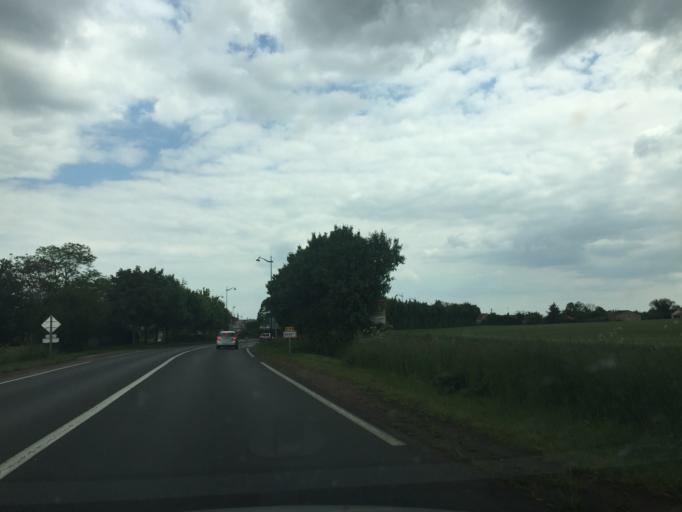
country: FR
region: Pays de la Loire
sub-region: Departement de la Vendee
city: Benet
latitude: 46.3780
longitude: -0.5986
